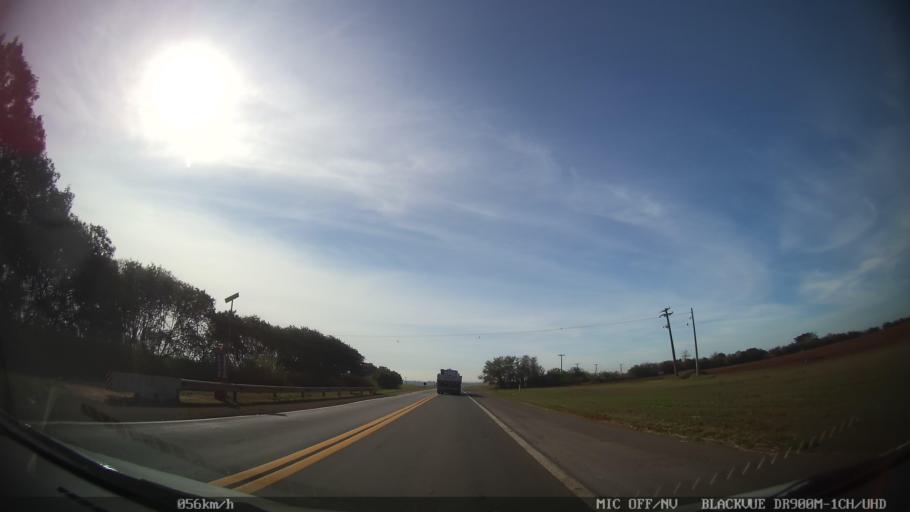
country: BR
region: Sao Paulo
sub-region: Rio Das Pedras
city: Rio das Pedras
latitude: -22.7945
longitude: -47.5857
